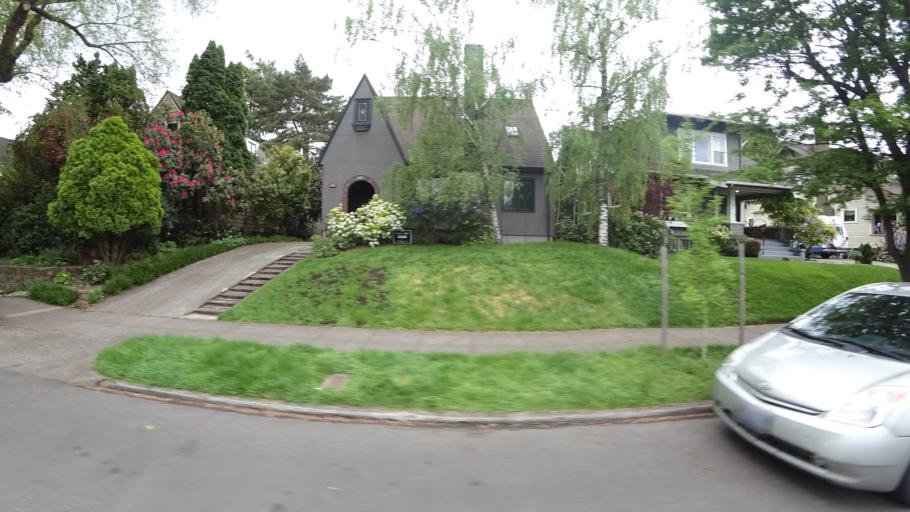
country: US
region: Oregon
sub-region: Multnomah County
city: Portland
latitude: 45.5476
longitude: -122.6208
